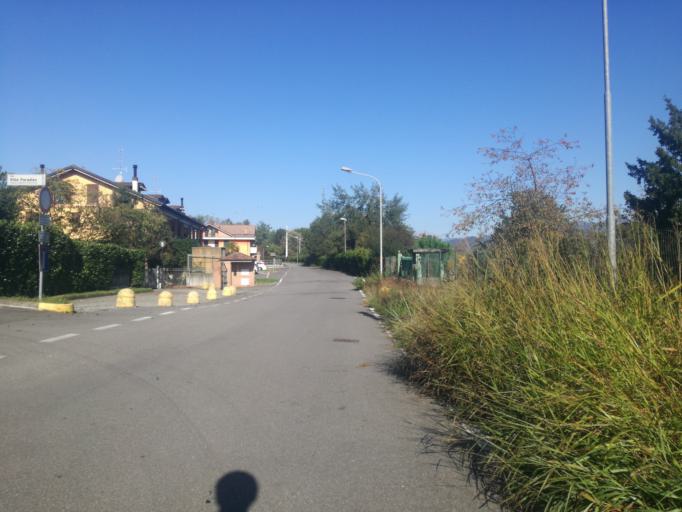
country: IT
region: Lombardy
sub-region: Provincia di Monza e Brianza
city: Porto d'Adda
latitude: 45.6498
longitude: 9.4837
